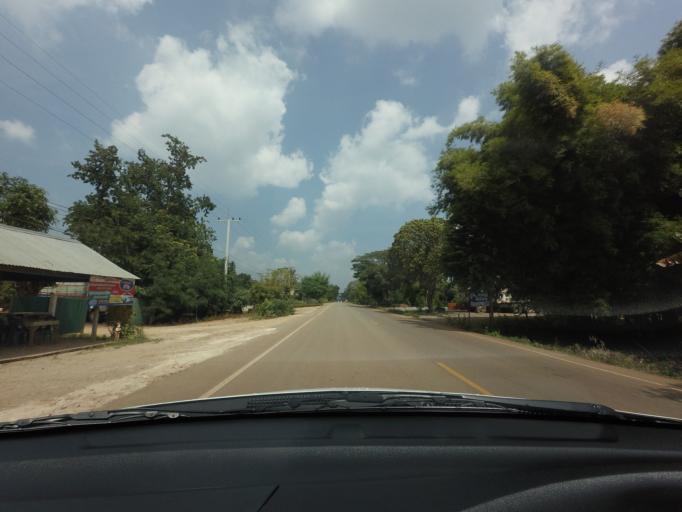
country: TH
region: Nakhon Ratchasima
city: Pak Chong
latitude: 14.5648
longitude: 101.5711
